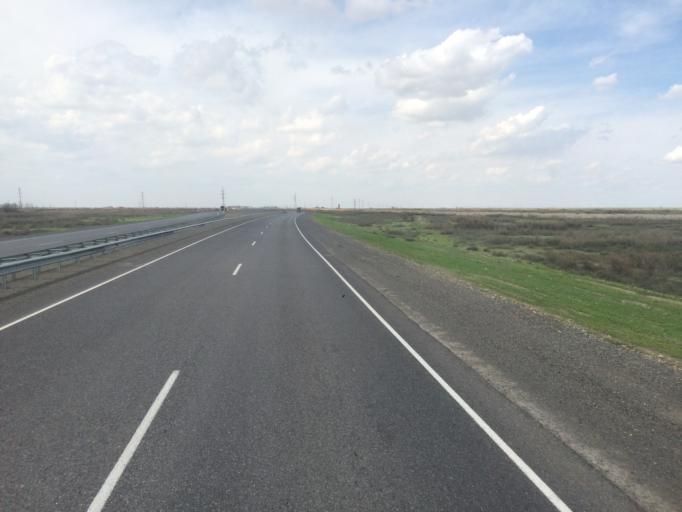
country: KZ
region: Qyzylorda
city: Zhangaqorghan
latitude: 43.9981
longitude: 67.2223
